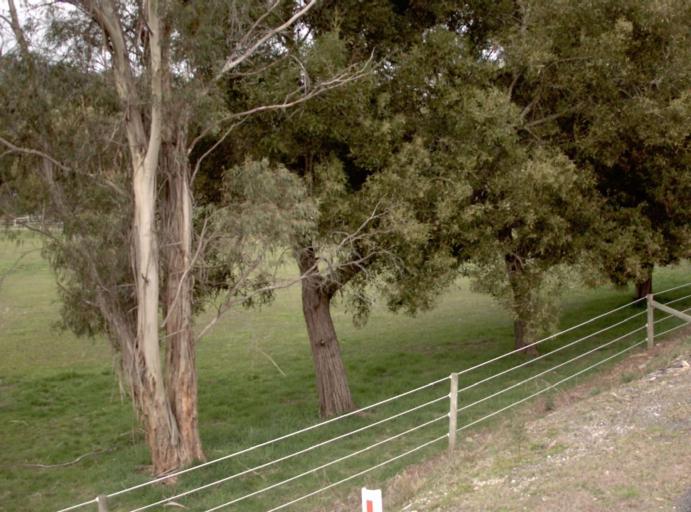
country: AU
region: Tasmania
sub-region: Launceston
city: Mayfield
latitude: -41.2631
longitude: 147.1605
